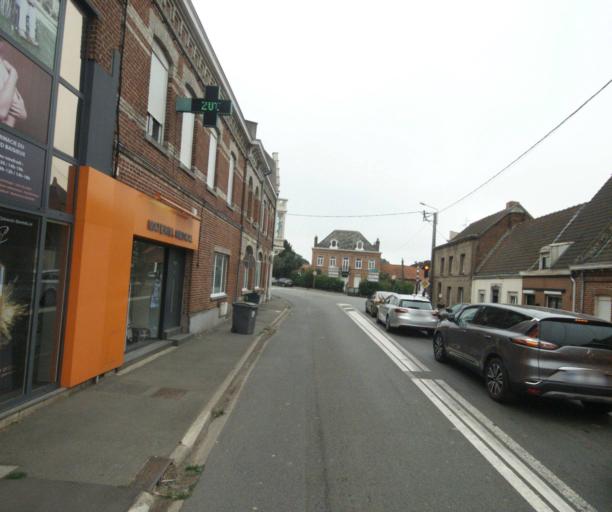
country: FR
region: Nord-Pas-de-Calais
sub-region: Departement du Nord
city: Baisieux
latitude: 50.6073
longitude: 3.2538
